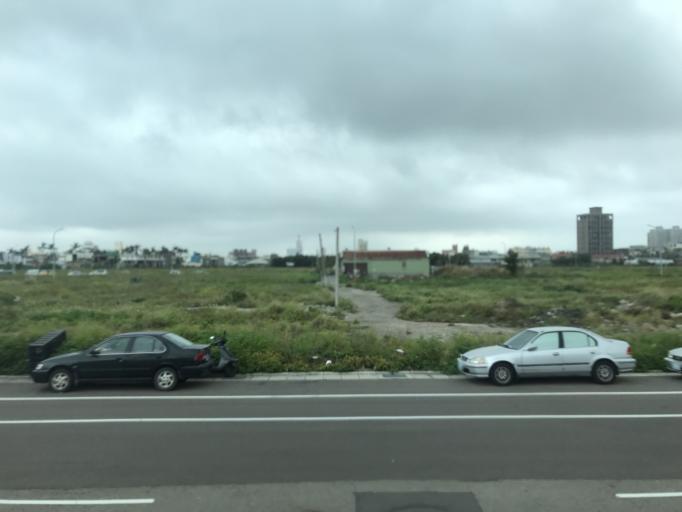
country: TW
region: Taiwan
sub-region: Hsinchu
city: Hsinchu
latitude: 24.8199
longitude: 120.9535
